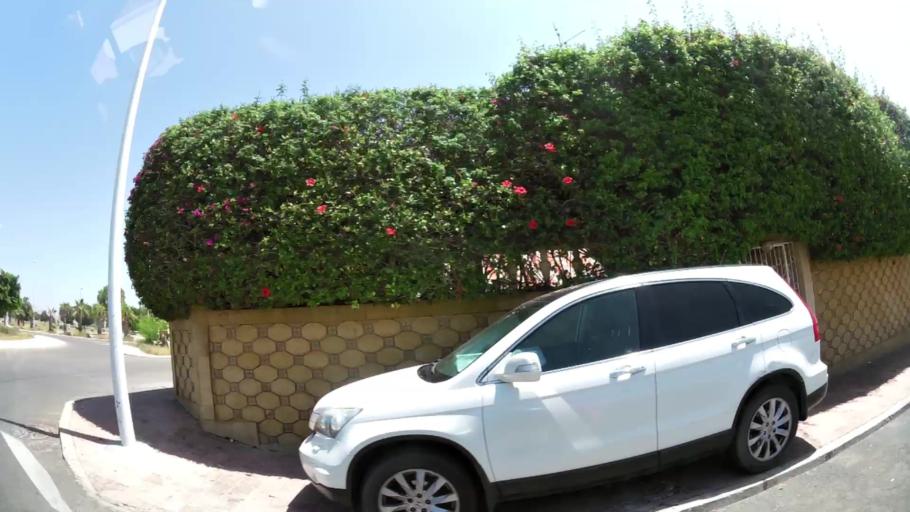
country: MA
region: Souss-Massa-Draa
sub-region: Agadir-Ida-ou-Tnan
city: Agadir
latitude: 30.4368
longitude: -9.5844
